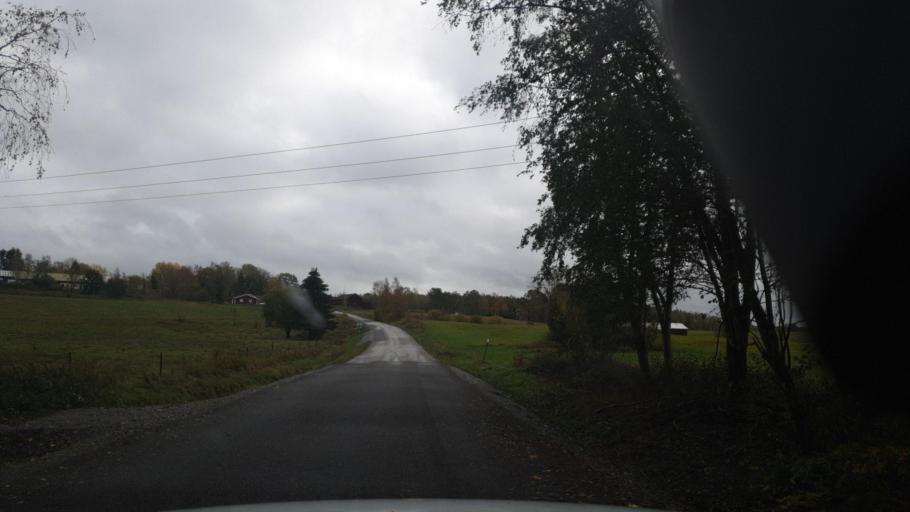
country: SE
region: Vaermland
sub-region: Karlstads Kommun
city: Valberg
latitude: 59.4215
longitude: 13.1029
